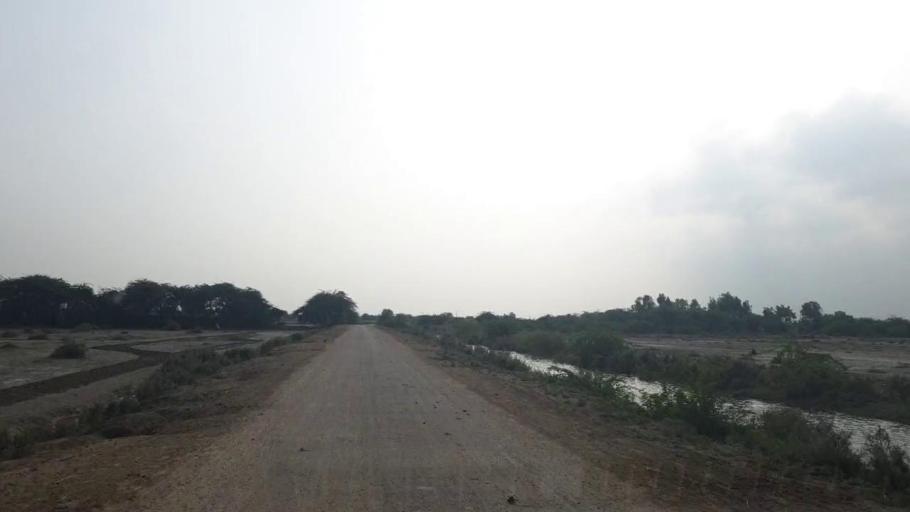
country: PK
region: Sindh
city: Badin
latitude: 24.6274
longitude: 68.6915
